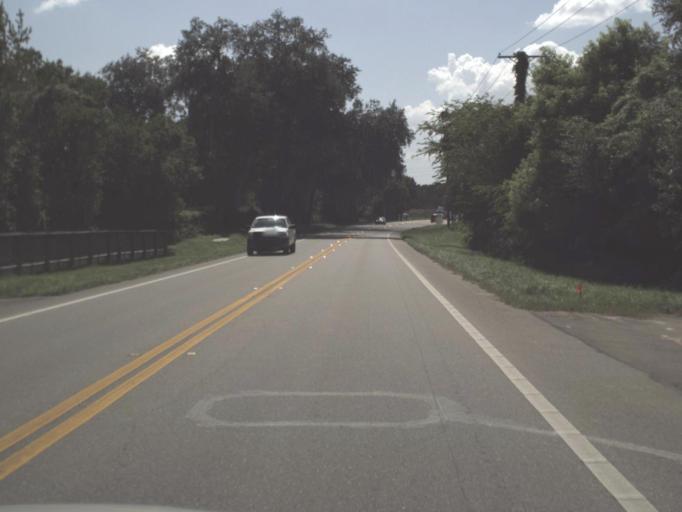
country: US
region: Florida
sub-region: Hillsborough County
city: Seffner
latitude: 28.0090
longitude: -82.2676
